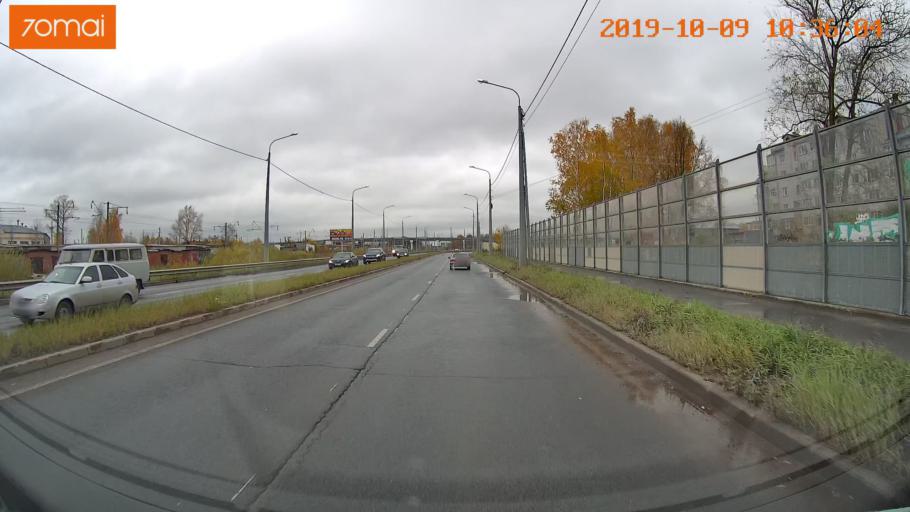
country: RU
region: Vologda
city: Vologda
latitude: 59.2305
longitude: 39.8634
